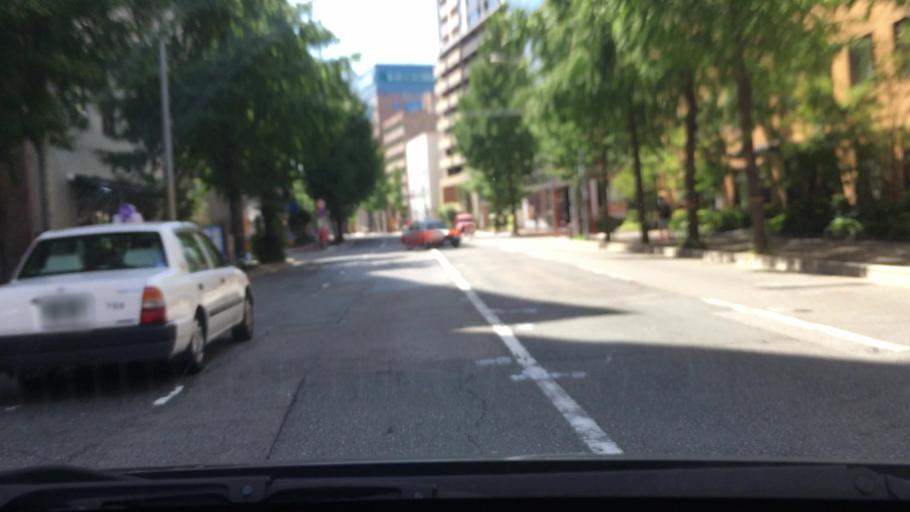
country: JP
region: Fukuoka
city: Fukuoka-shi
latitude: 33.5891
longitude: 130.4131
